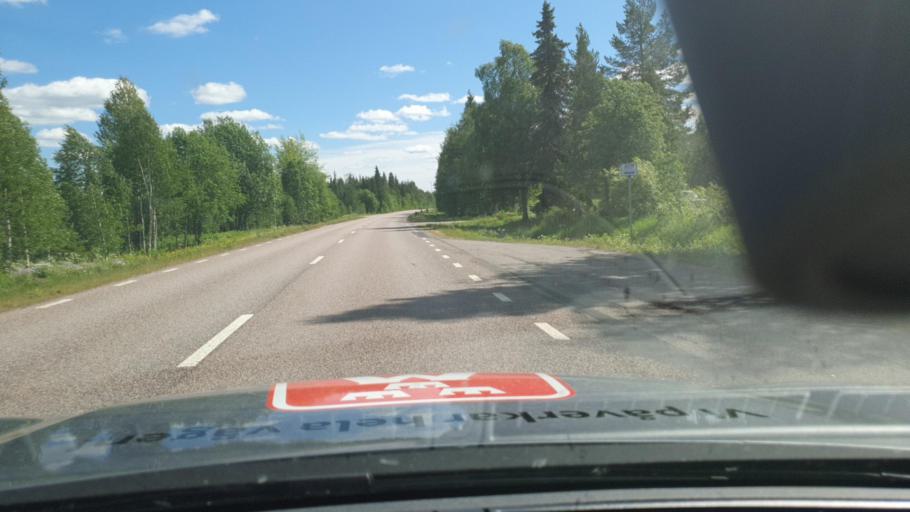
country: FI
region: Lapland
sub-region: Tunturi-Lappi
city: Kolari
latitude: 67.1083
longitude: 23.6383
